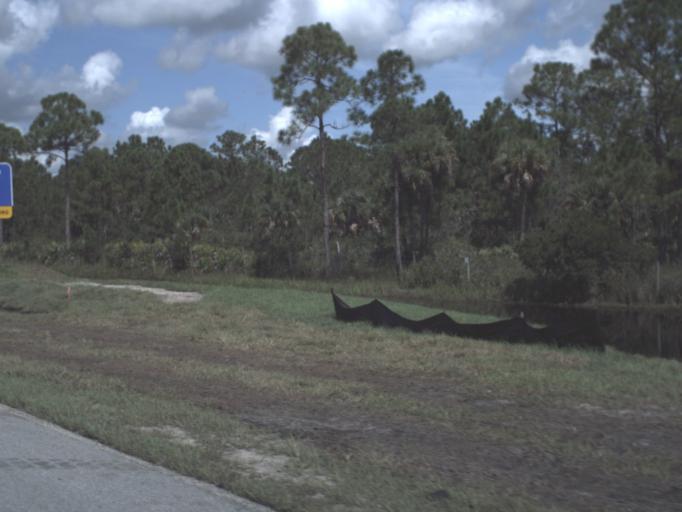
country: US
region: Florida
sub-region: Sarasota County
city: Warm Mineral Springs
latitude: 27.1094
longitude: -82.3074
